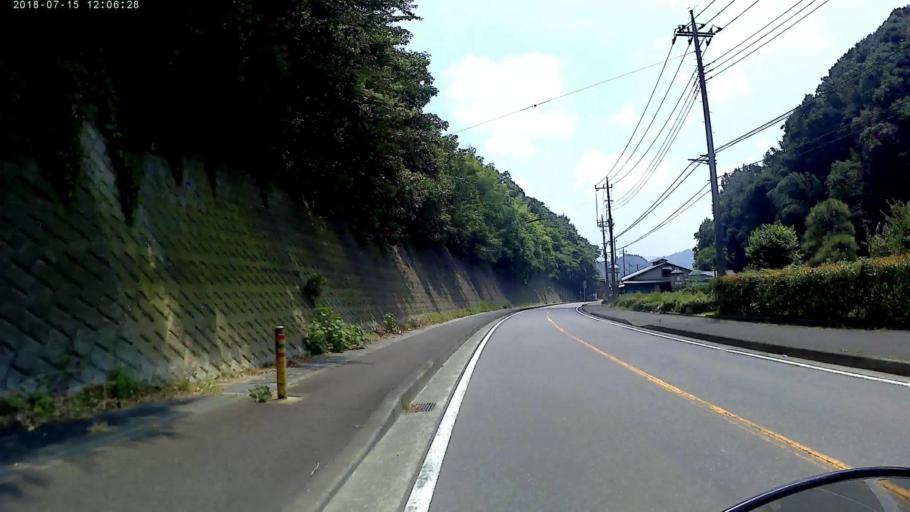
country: JP
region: Kanagawa
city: Hadano
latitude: 35.3341
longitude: 139.2200
